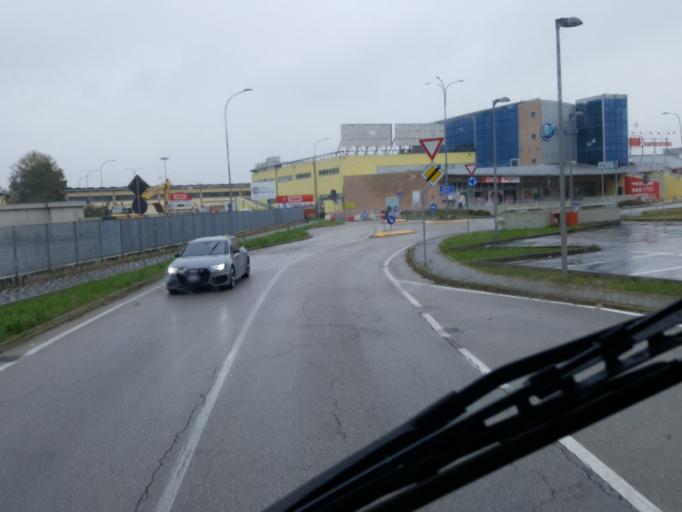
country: IT
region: Veneto
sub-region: Provincia di Treviso
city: Mogliano Veneto
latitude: 45.5556
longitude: 12.2262
